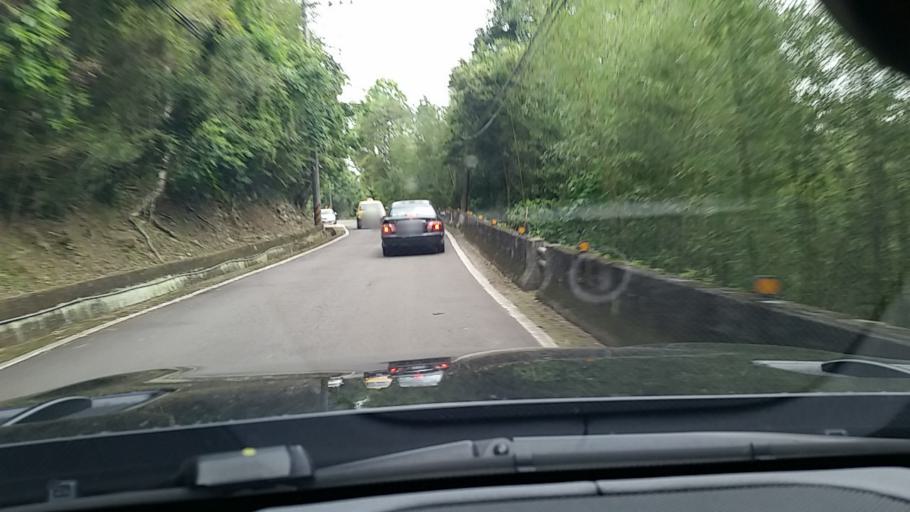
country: TW
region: Taiwan
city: Daxi
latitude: 24.7999
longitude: 121.3047
